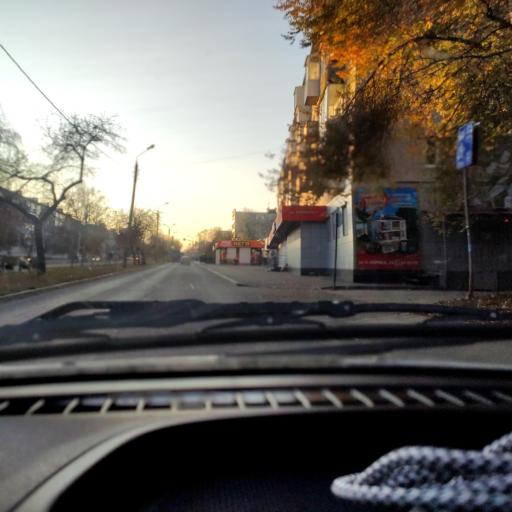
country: RU
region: Samara
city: Tol'yatti
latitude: 53.5201
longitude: 49.4020
